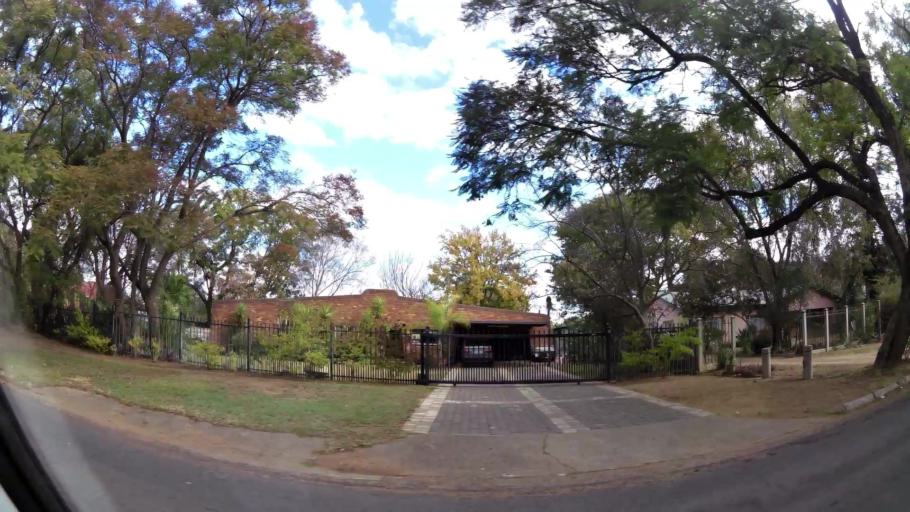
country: ZA
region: Limpopo
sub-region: Waterberg District Municipality
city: Modimolle
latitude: -24.7094
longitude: 28.4041
